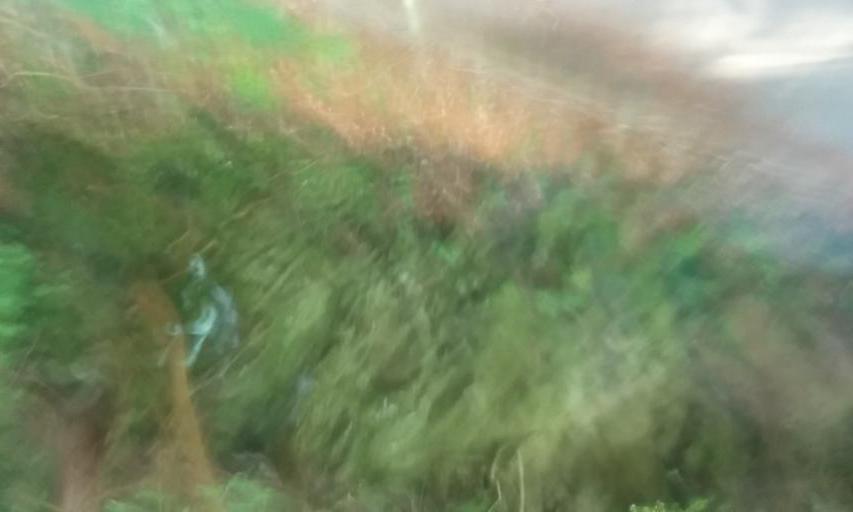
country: JP
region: Ehime
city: Niihama
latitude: 33.8757
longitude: 133.2959
